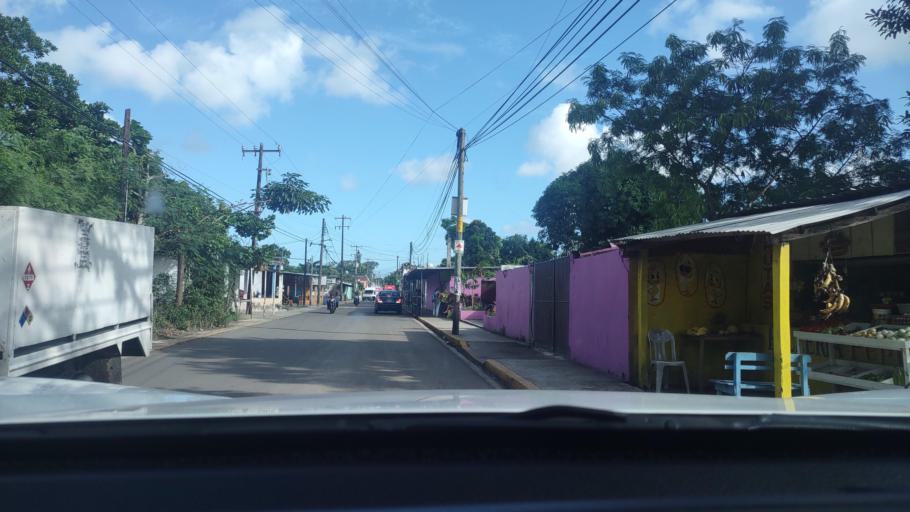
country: MX
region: Veracruz
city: El Tejar
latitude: 19.0753
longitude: -96.1644
